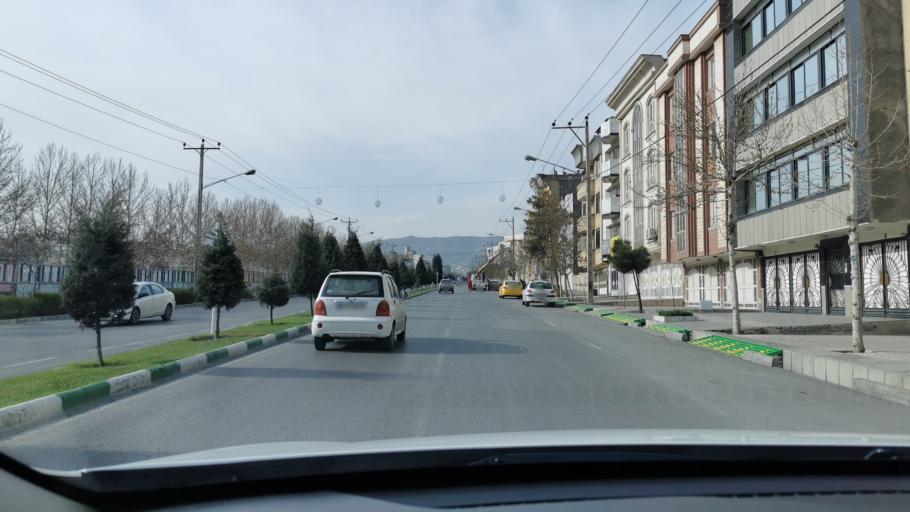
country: IR
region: Razavi Khorasan
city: Mashhad
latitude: 36.3097
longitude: 59.5154
